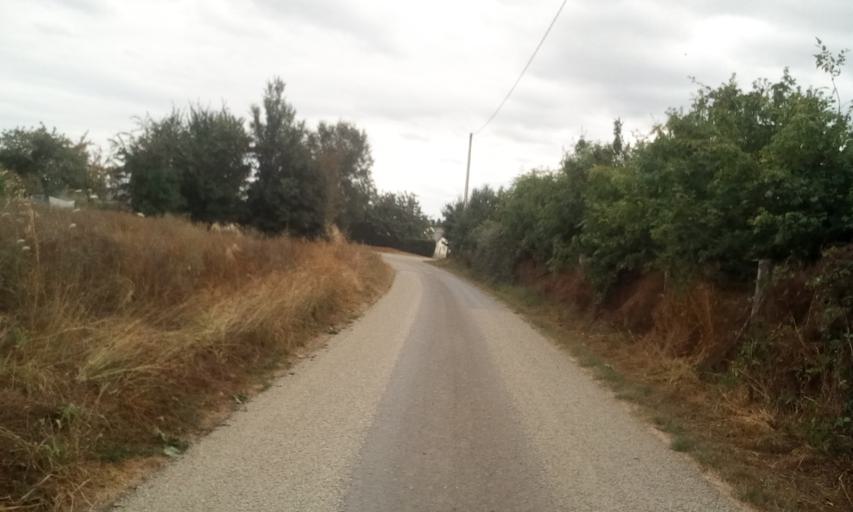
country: FR
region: Lower Normandy
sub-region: Departement du Calvados
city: Thury-Harcourt
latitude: 48.9892
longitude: -0.4279
